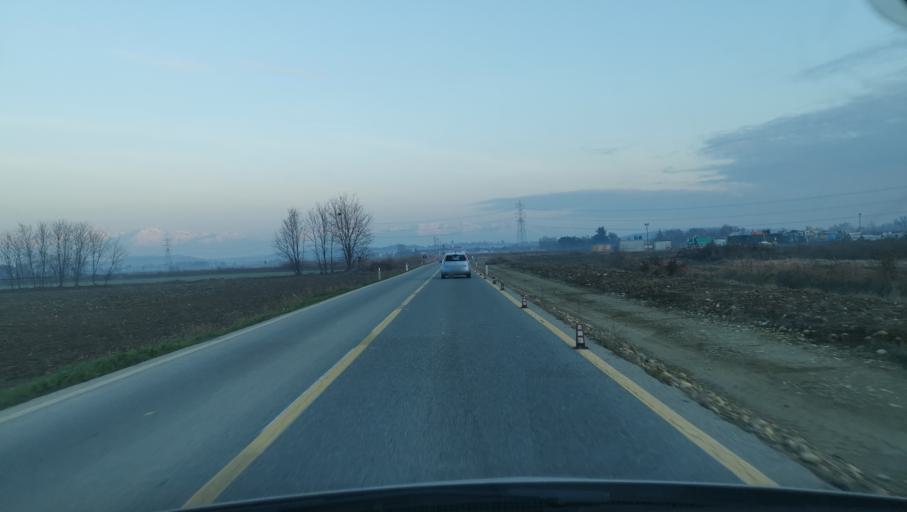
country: IT
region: Piedmont
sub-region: Provincia di Torino
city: Caluso
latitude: 45.2718
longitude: 7.8925
